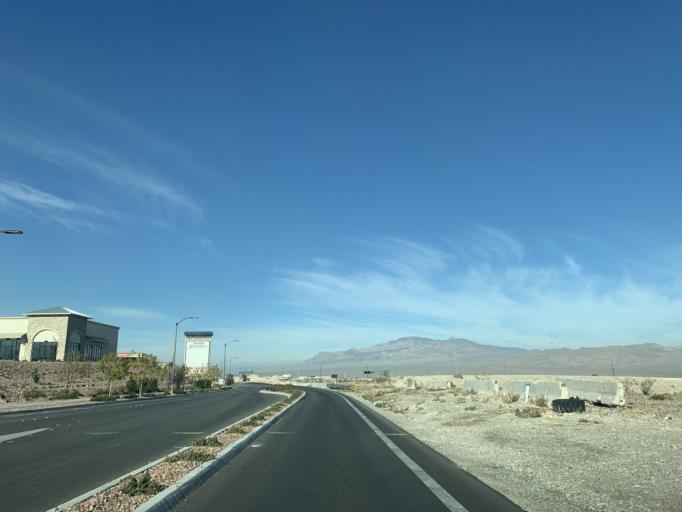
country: US
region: Nevada
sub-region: Clark County
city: Summerlin South
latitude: 36.3149
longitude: -115.3059
